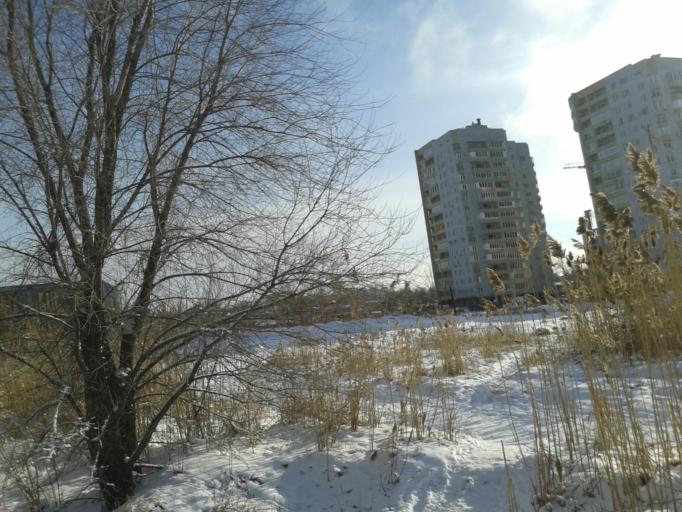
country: RU
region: Volgograd
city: Volgograd
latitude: 48.7469
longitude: 44.5000
